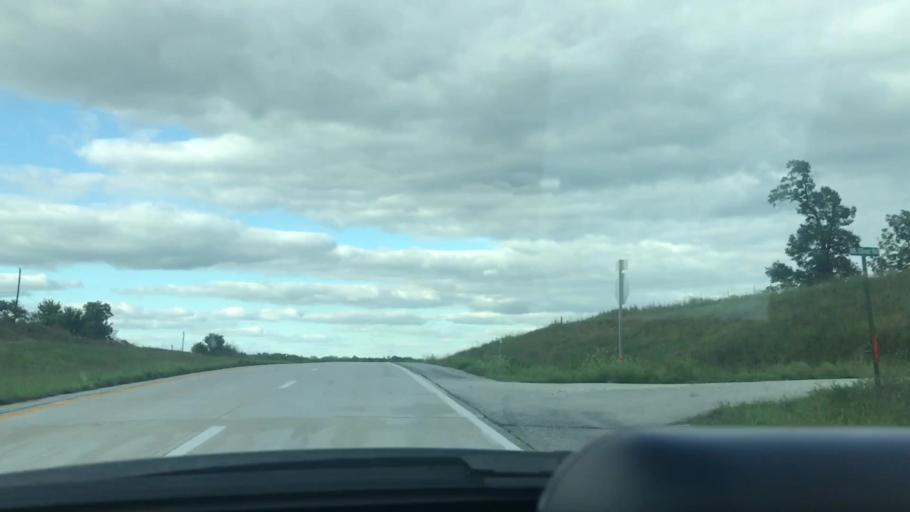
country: US
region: Missouri
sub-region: Benton County
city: Lincoln
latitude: 38.4409
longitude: -93.2971
